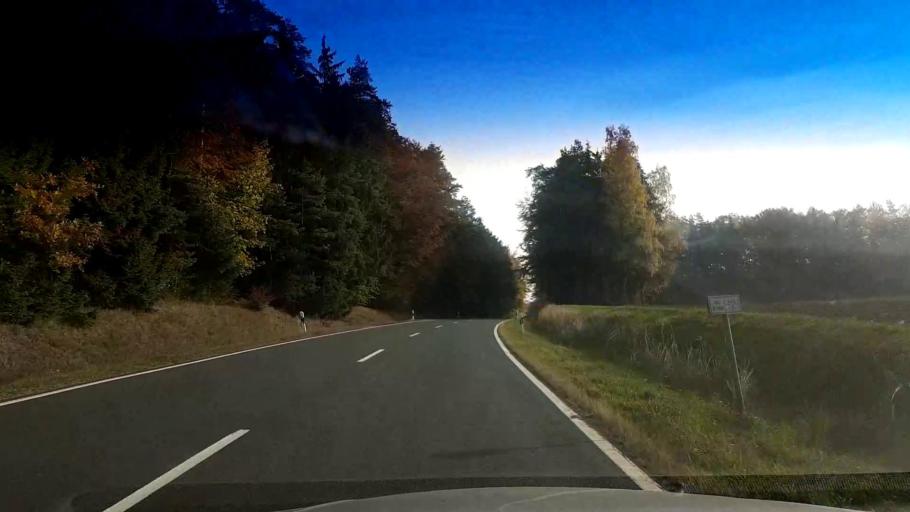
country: DE
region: Bavaria
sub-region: Upper Franconia
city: Wattendorf
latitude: 49.9990
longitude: 11.1444
